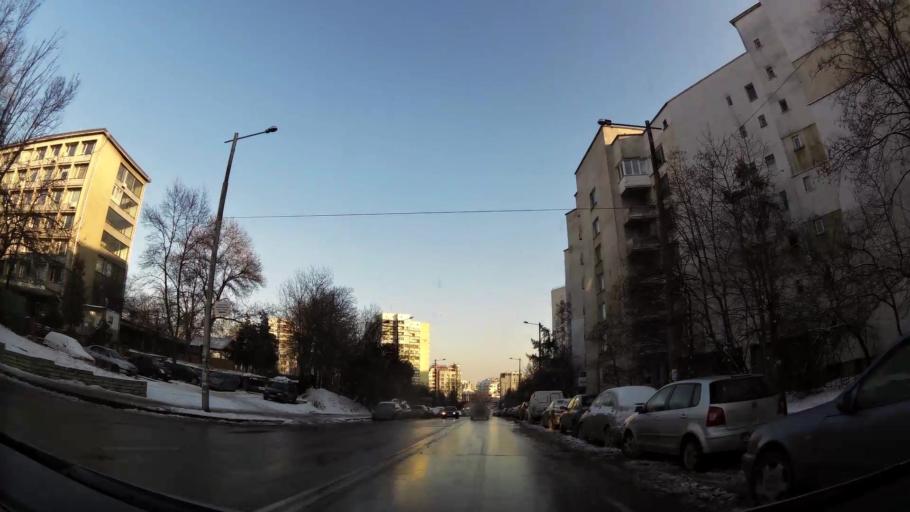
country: BG
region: Sofia-Capital
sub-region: Stolichna Obshtina
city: Sofia
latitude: 42.6820
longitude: 23.3685
